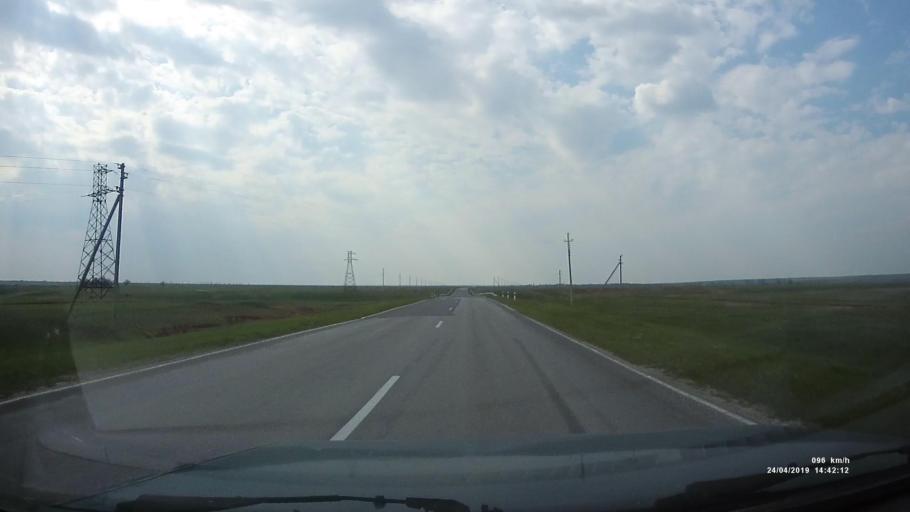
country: RU
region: Rostov
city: Remontnoye
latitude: 46.4508
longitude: 43.8669
